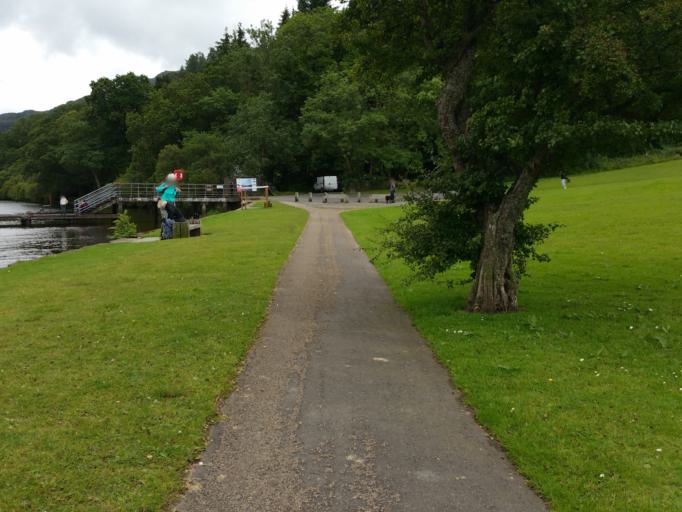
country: GB
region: Scotland
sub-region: Argyll and Bute
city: Garelochhead
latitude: 56.2033
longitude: -4.7082
